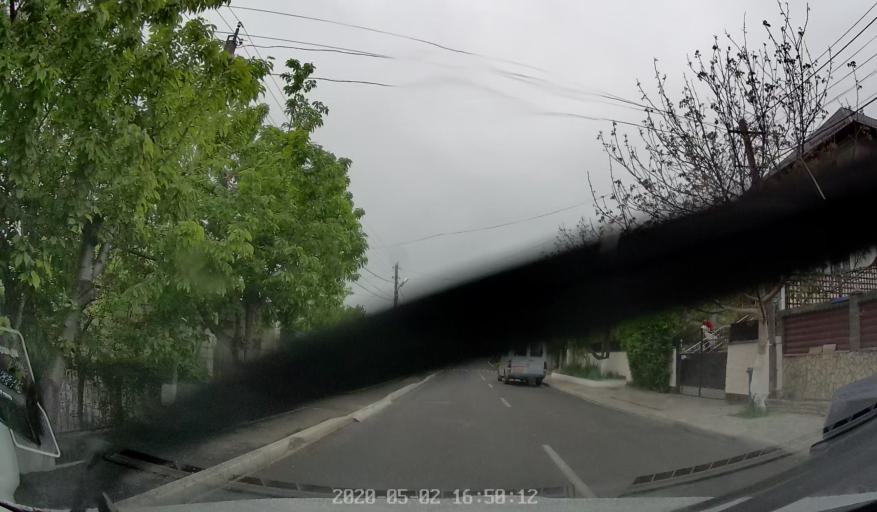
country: MD
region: Chisinau
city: Chisinau
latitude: 46.9670
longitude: 28.8286
